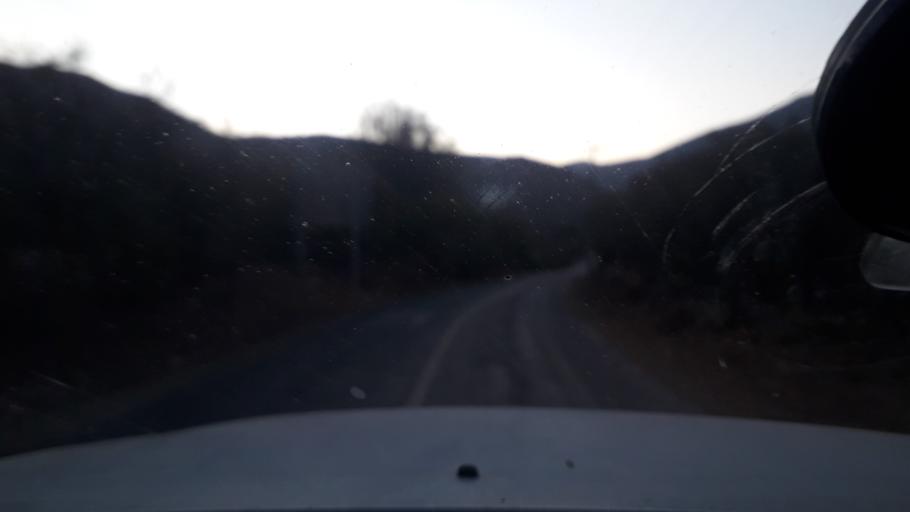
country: CL
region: Valparaiso
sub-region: Provincia de Marga Marga
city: Limache
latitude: -33.1768
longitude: -71.1243
